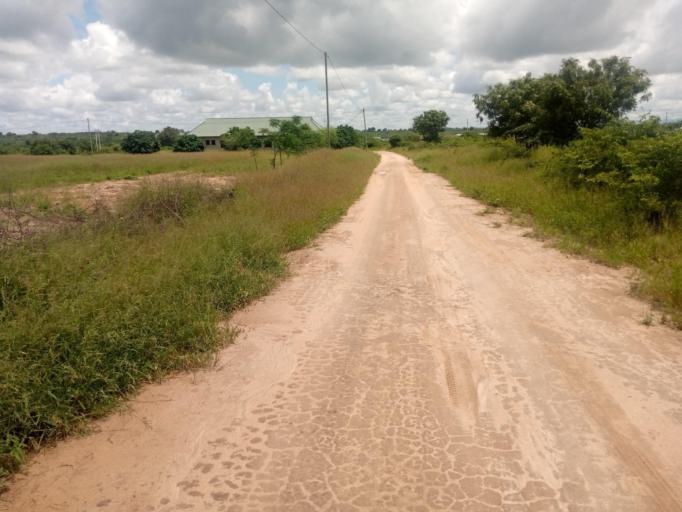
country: TZ
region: Dodoma
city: Dodoma
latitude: -6.1138
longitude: 35.7393
